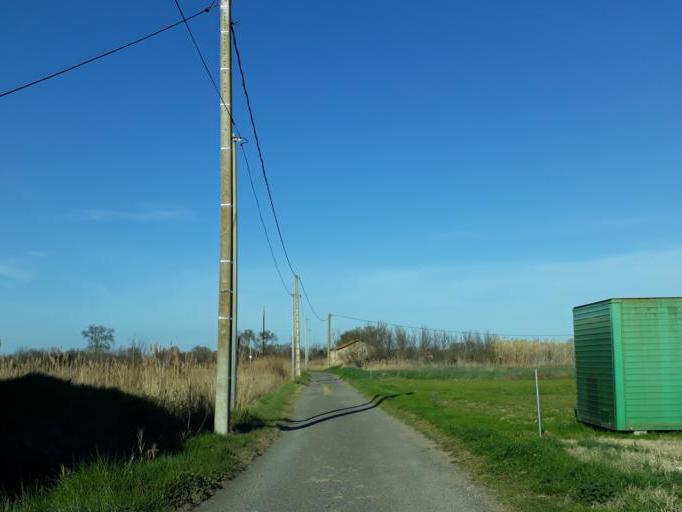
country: FR
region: Languedoc-Roussillon
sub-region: Departement de l'Herault
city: Agde
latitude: 43.3230
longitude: 3.4565
